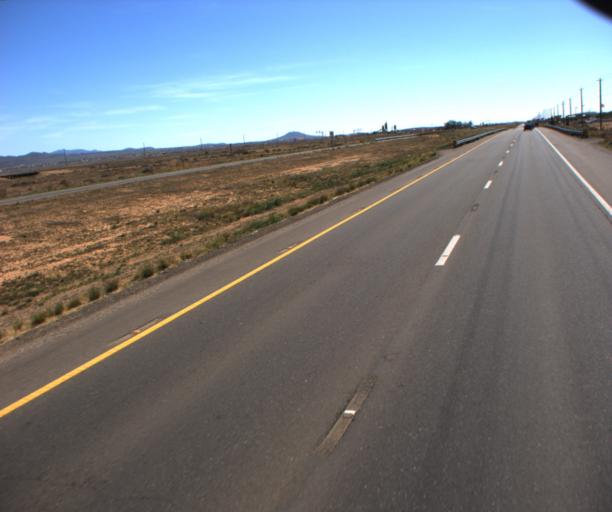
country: US
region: Arizona
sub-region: Mohave County
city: New Kingman-Butler
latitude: 35.2607
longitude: -113.9693
